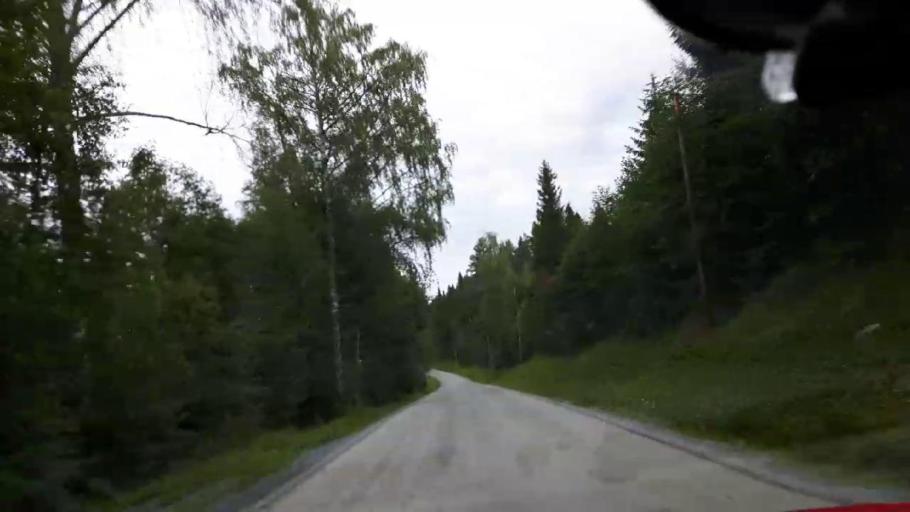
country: SE
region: Jaemtland
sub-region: Braecke Kommun
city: Braecke
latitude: 63.0874
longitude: 15.2625
